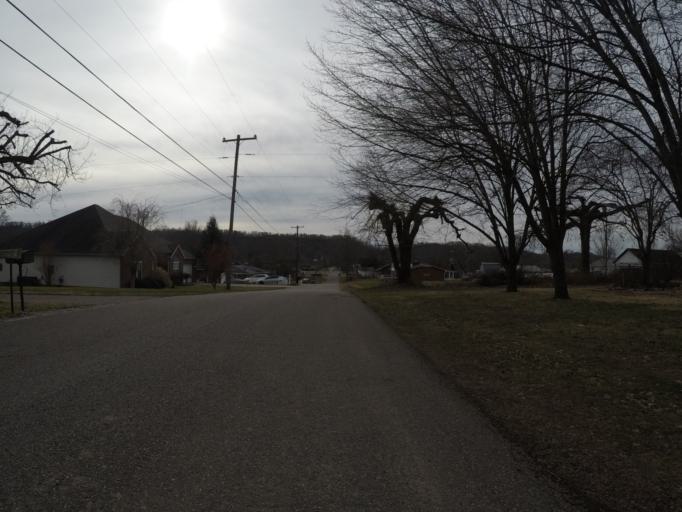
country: US
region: West Virginia
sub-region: Cabell County
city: Pea Ridge
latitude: 38.4455
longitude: -82.3533
